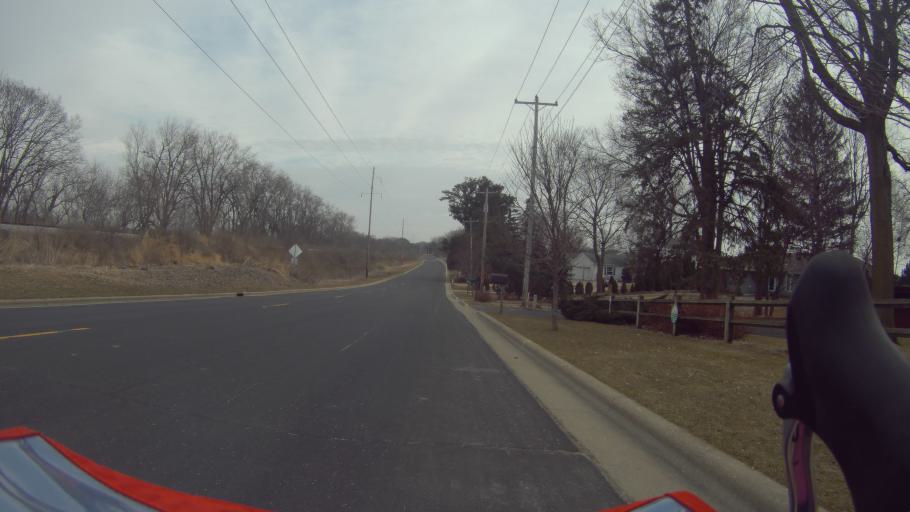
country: US
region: Wisconsin
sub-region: Dane County
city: Maple Bluff
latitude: 43.1299
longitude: -89.3806
